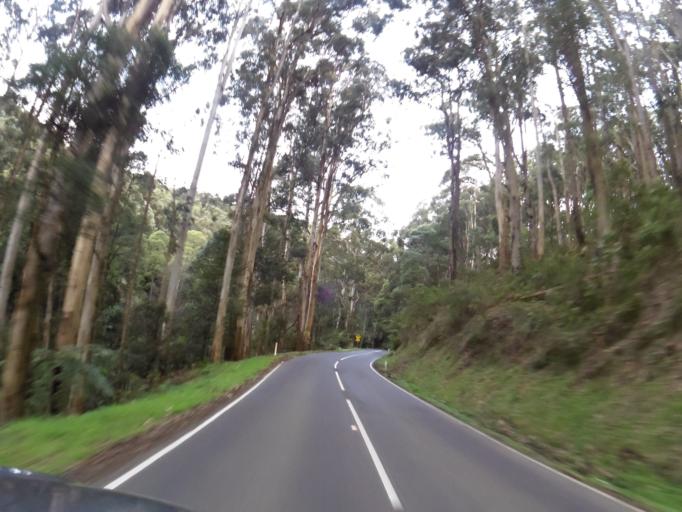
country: AU
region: Victoria
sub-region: Yarra Ranges
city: Ferny Creek
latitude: -37.8645
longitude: 145.3432
